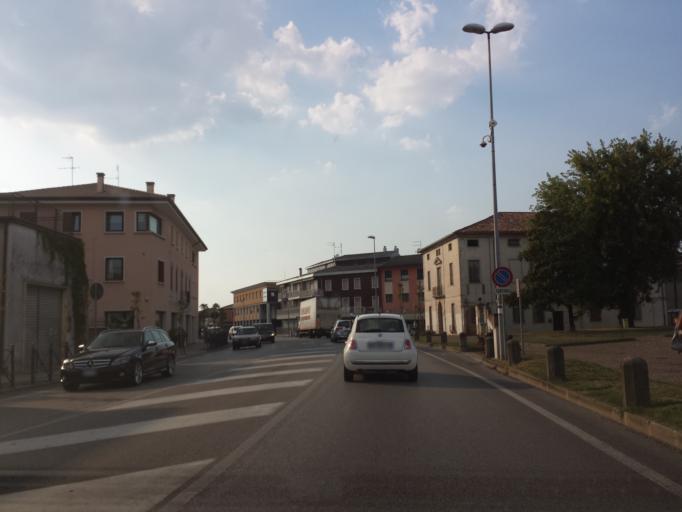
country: IT
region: Veneto
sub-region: Provincia di Padova
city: Mestrino
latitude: 45.4429
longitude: 11.7579
